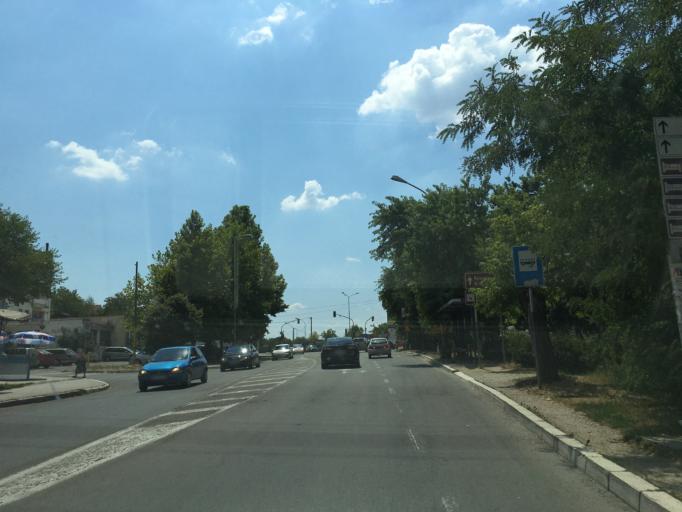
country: RS
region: Central Serbia
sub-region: Belgrade
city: Mladenovac
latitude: 44.4484
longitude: 20.6866
